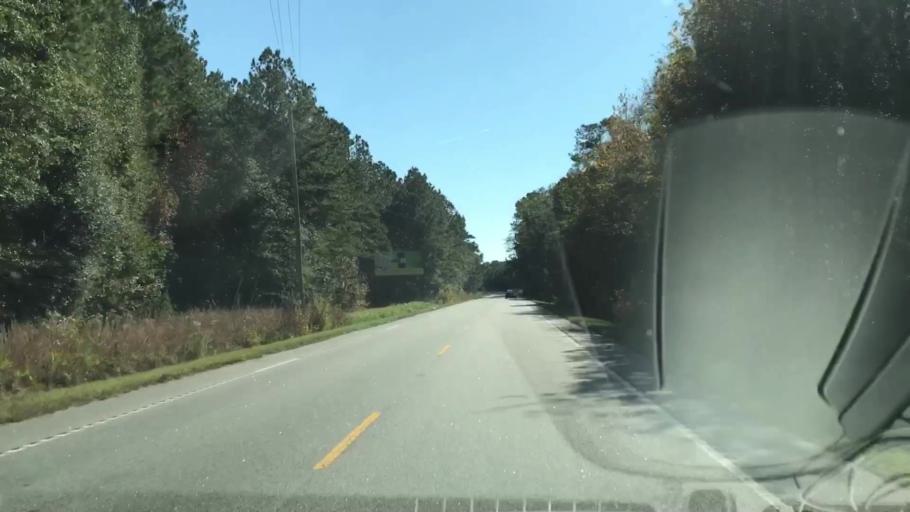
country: US
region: South Carolina
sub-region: Jasper County
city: Ridgeland
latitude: 32.5282
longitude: -80.9002
